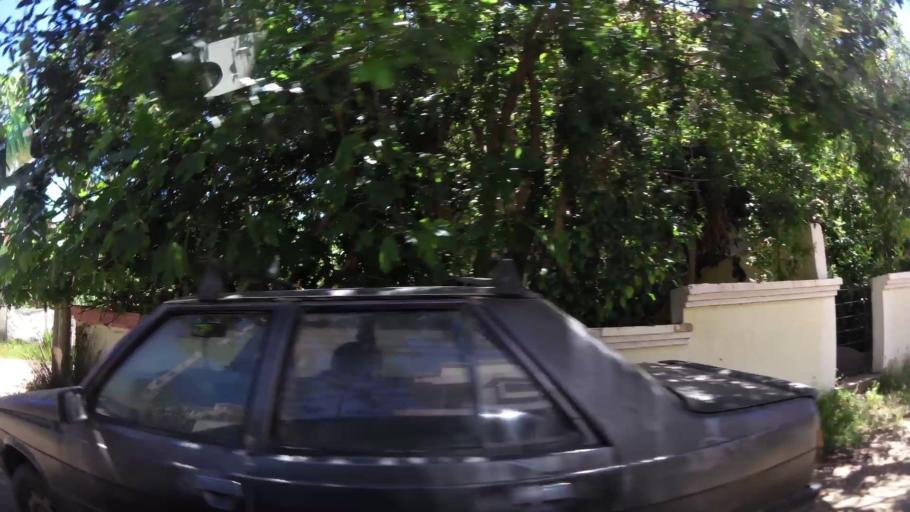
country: MA
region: Oriental
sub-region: Berkane-Taourirt
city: Madagh
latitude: 35.0851
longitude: -2.2404
